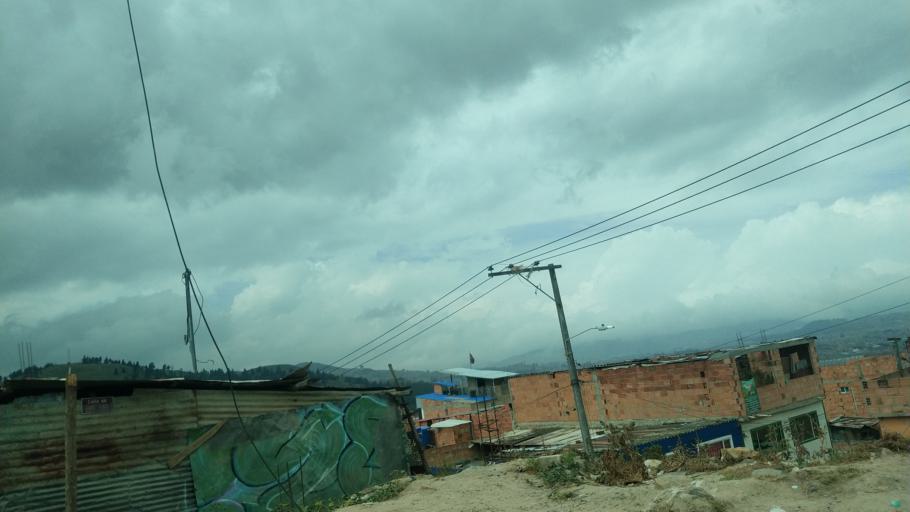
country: CO
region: Cundinamarca
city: Soacha
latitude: 4.5828
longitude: -74.1861
